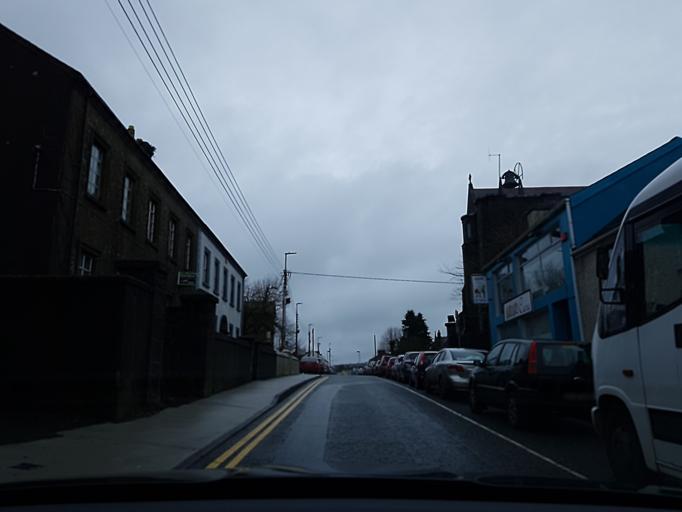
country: IE
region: Connaught
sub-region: Maigh Eo
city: Castlebar
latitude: 53.8577
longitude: -9.3018
